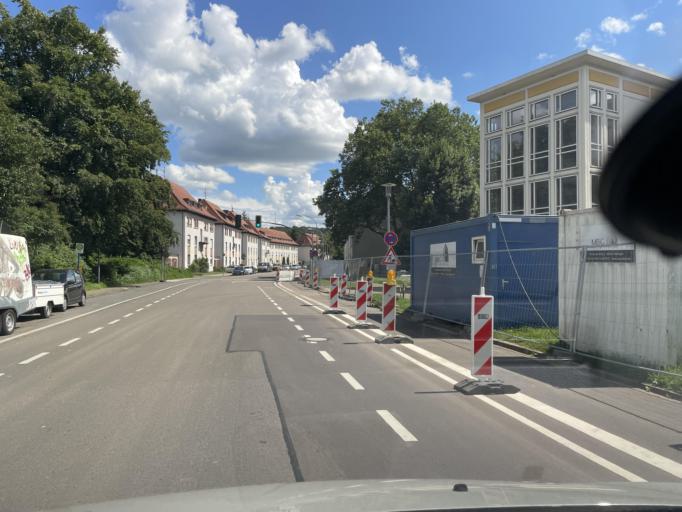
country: DE
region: Saarland
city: Saarbrucken
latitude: 49.2323
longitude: 7.0147
